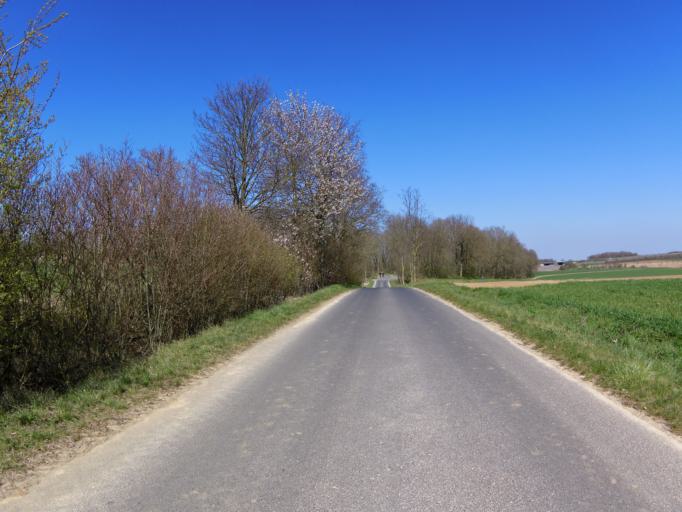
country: DE
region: Bavaria
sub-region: Regierungsbezirk Unterfranken
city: Biebelried
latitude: 49.7725
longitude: 10.0811
